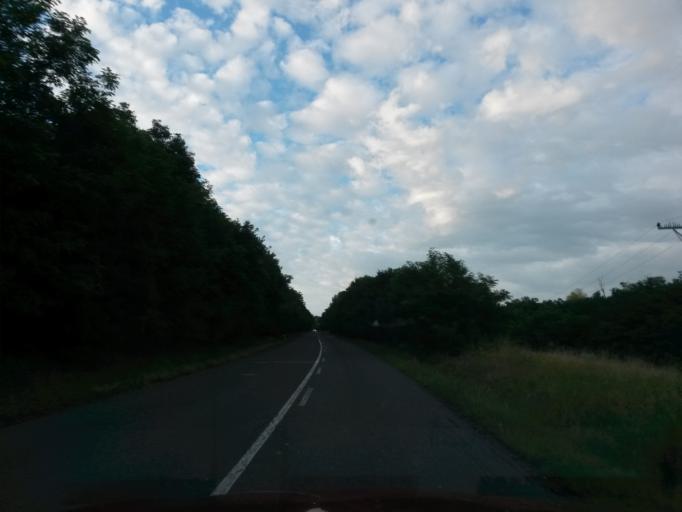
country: SK
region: Banskobystricky
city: Lucenec
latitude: 48.3129
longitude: 19.5258
